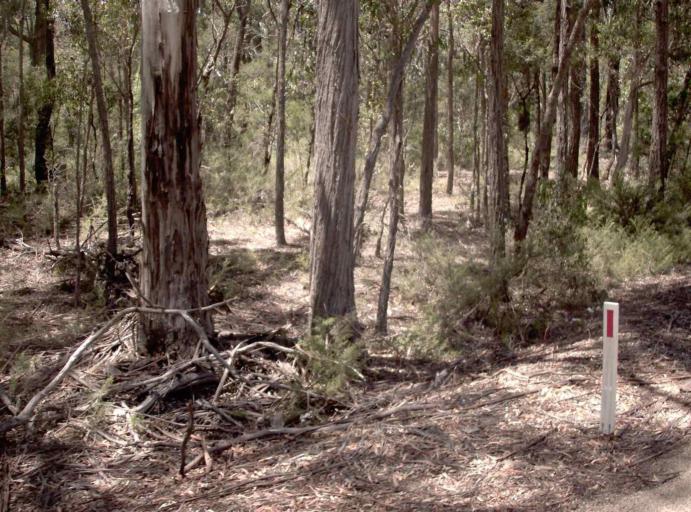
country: AU
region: Victoria
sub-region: East Gippsland
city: Lakes Entrance
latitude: -37.6262
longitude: 147.8851
